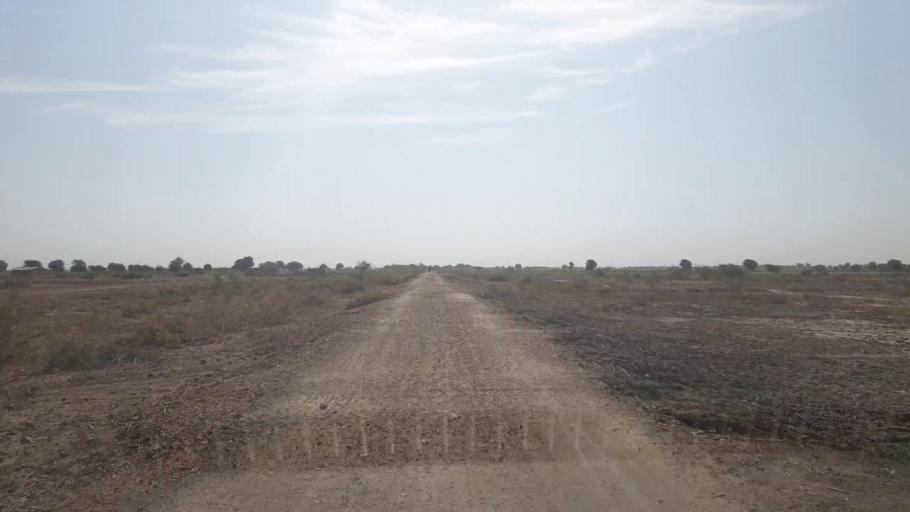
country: PK
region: Sindh
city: Umarkot
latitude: 25.2820
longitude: 69.6590
